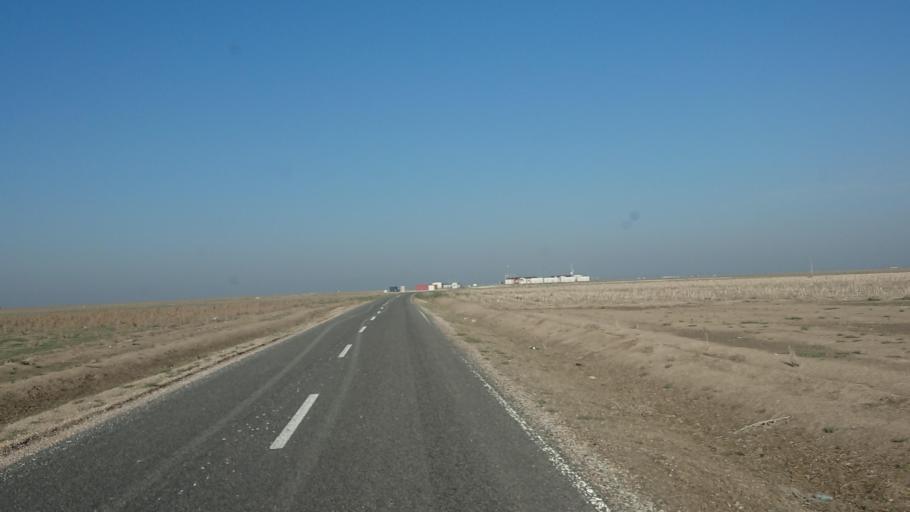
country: TR
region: Aksaray
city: Yesilova
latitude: 38.3879
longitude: 33.7523
